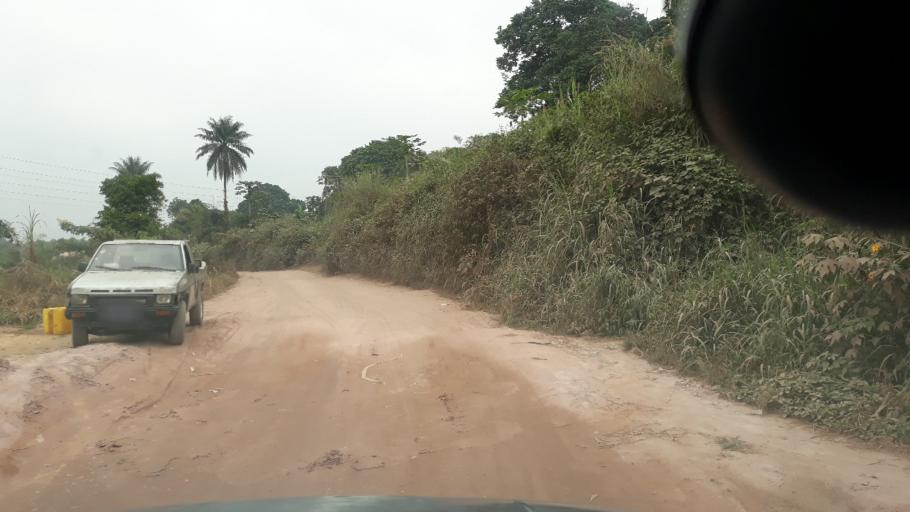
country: CD
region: Kinshasa
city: Masina
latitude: -4.4757
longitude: 15.2766
